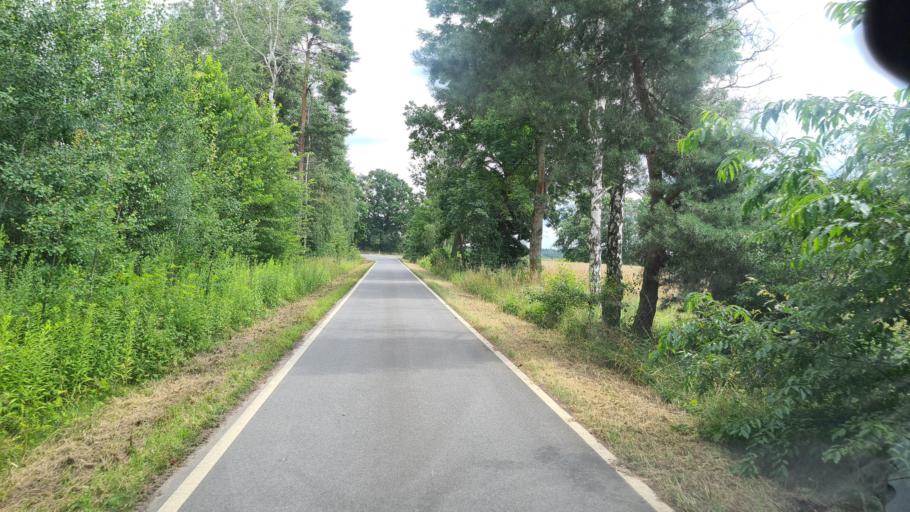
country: DE
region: Brandenburg
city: Grossraschen
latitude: 51.5681
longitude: 14.0756
